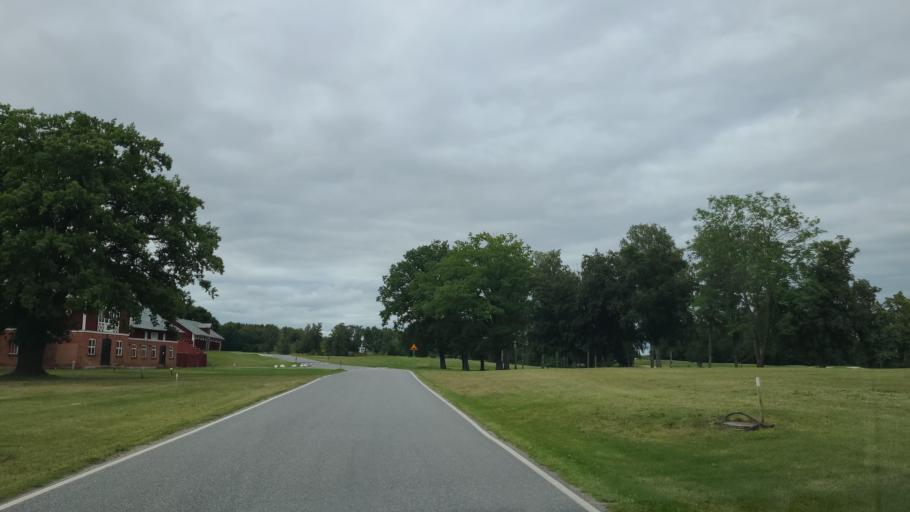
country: SE
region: Stockholm
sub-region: Upplands-Bro Kommun
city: Bro
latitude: 59.4980
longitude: 17.6266
